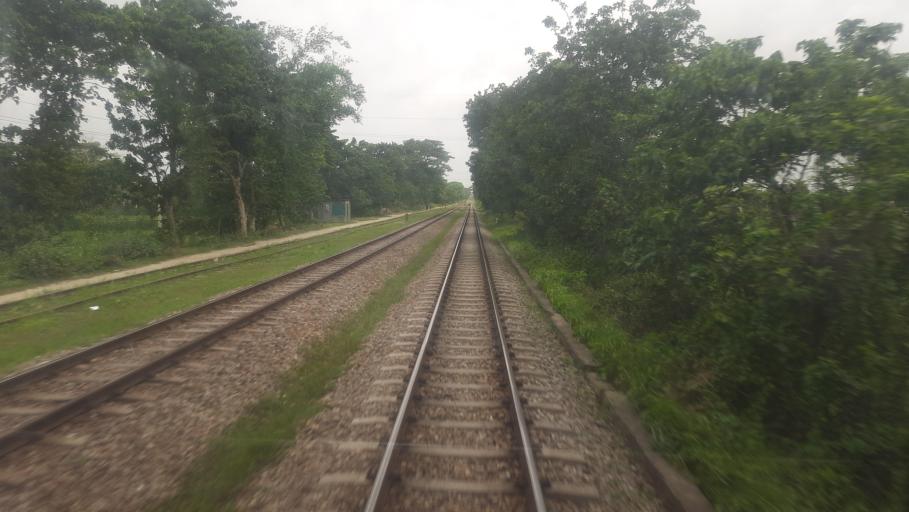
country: BD
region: Dhaka
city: Bhairab Bazar
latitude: 24.0275
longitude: 91.0158
